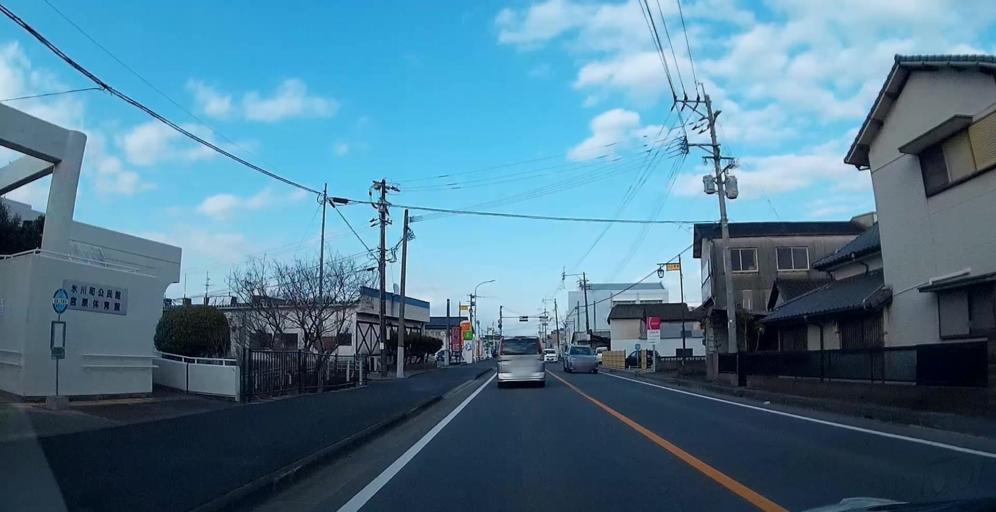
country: JP
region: Kumamoto
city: Yatsushiro
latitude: 32.5538
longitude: 130.6801
